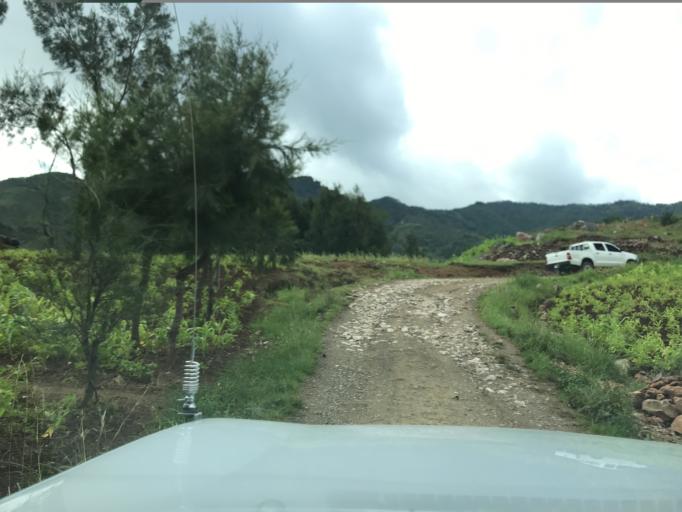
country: TL
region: Aileu
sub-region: Aileu Villa
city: Aileu
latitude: -8.8600
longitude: 125.5722
